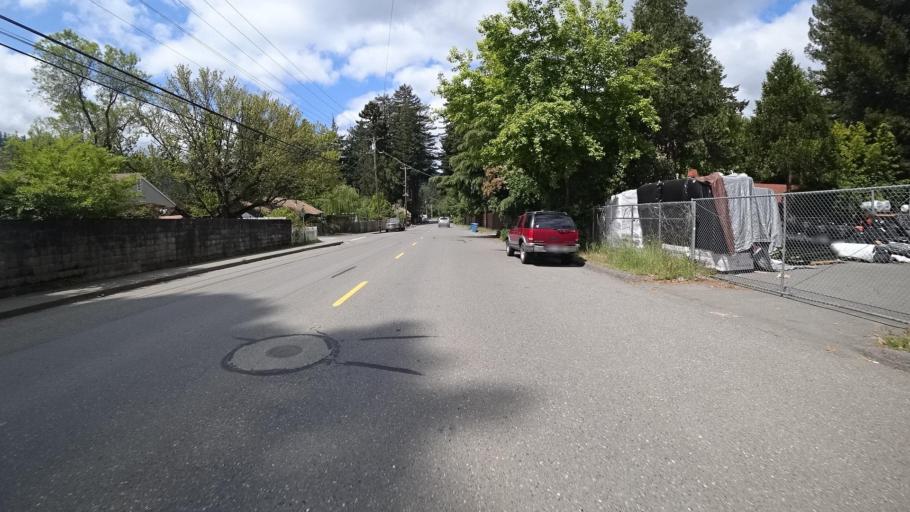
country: US
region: California
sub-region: Humboldt County
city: Redway
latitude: 40.1209
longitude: -123.8275
